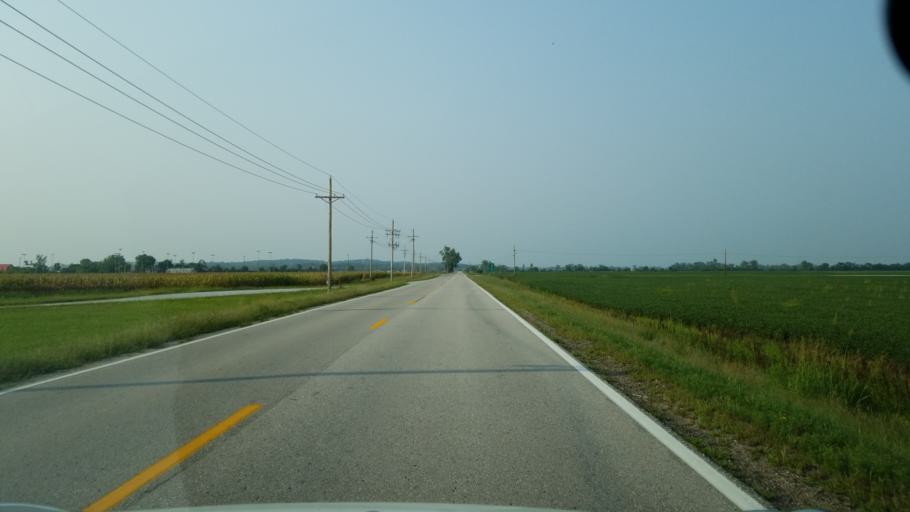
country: US
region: Nebraska
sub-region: Sarpy County
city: Offutt Air Force Base
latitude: 41.0981
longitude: -95.8899
